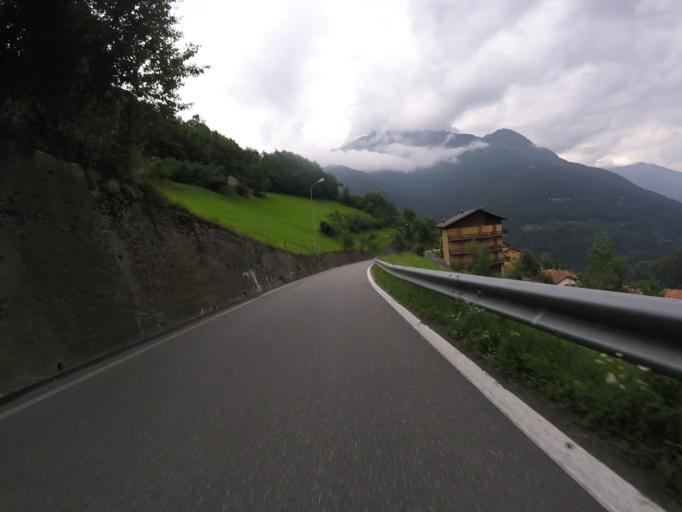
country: IT
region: Lombardy
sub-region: Provincia di Brescia
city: Monno
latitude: 46.2131
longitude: 10.3423
